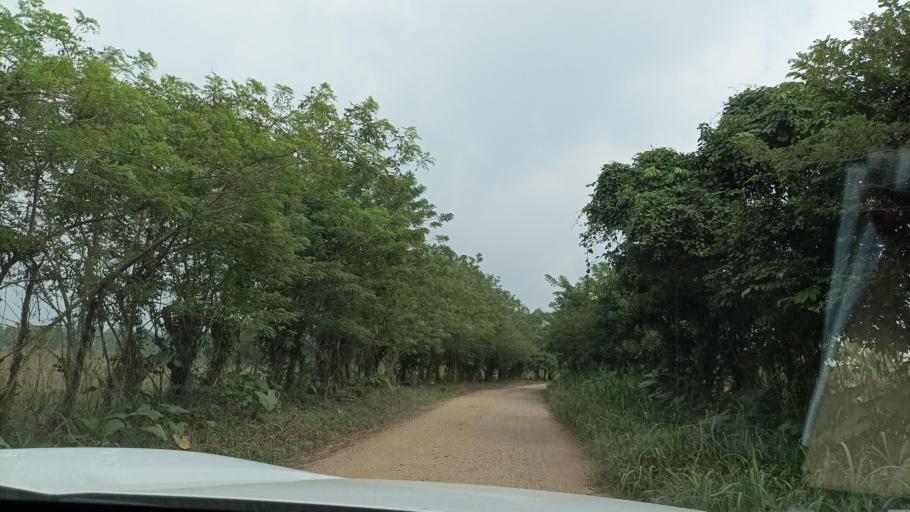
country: MX
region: Veracruz
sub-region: Moloacan
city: Cuichapa
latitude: 17.5832
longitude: -94.2186
